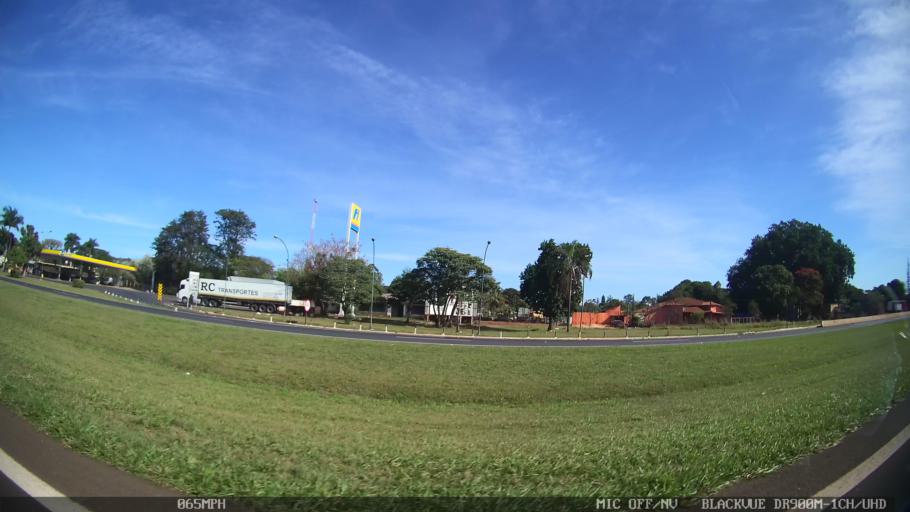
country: BR
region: Sao Paulo
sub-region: Leme
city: Leme
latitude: -22.2240
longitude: -47.3916
